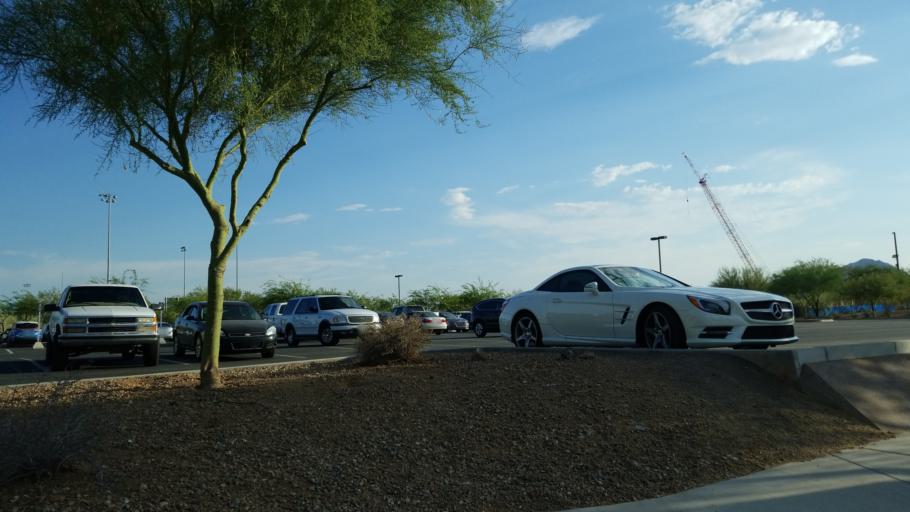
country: US
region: Arizona
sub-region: Maricopa County
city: Scottsdale
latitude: 33.5458
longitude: -111.8877
